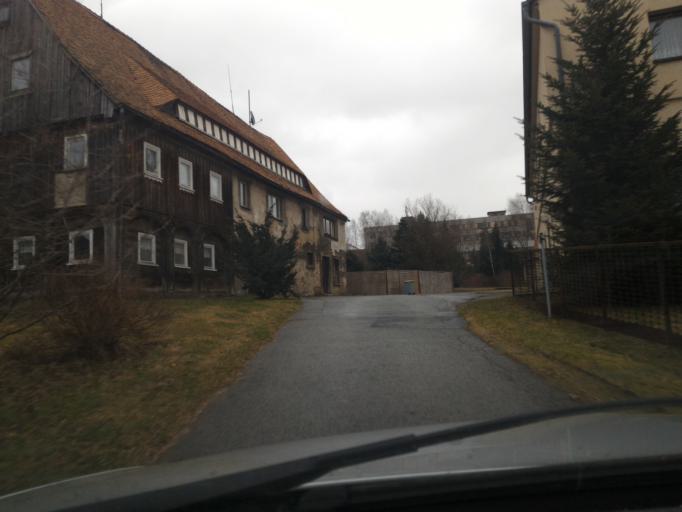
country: DE
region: Saxony
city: Seifhennersdorf
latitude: 50.9338
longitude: 14.6200
